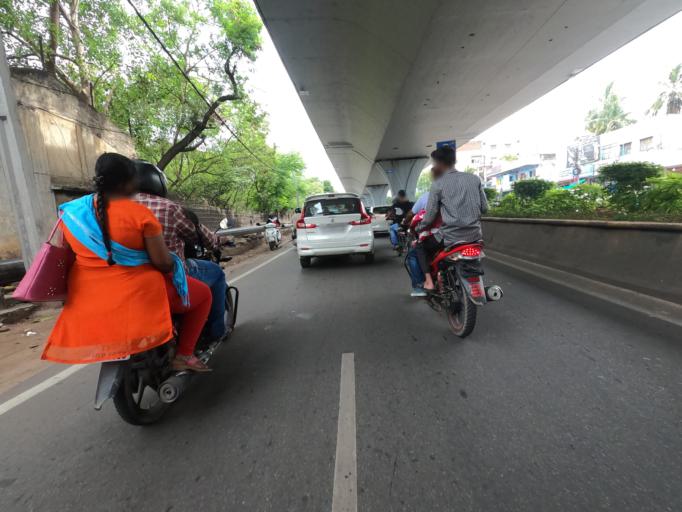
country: IN
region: Telangana
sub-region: Hyderabad
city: Hyderabad
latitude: 17.3854
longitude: 78.4295
